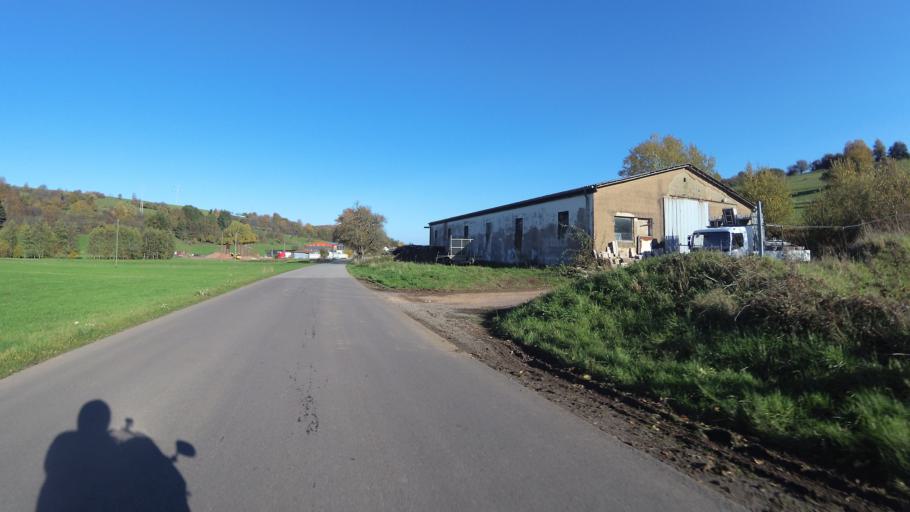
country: DE
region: Saarland
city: Losheim
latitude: 49.4873
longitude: 6.7646
